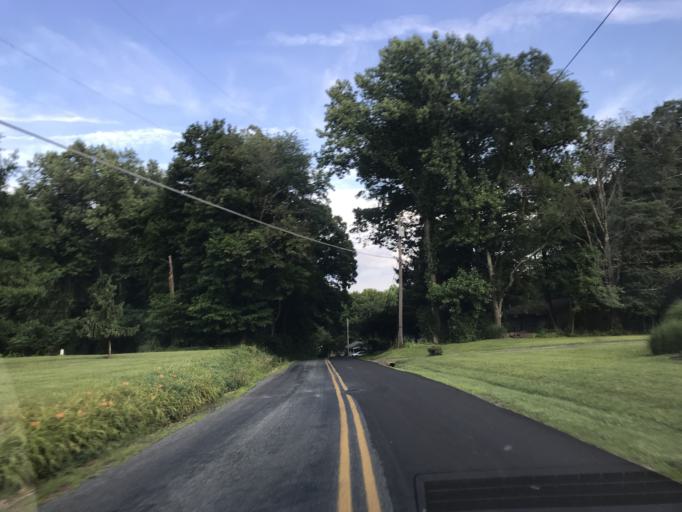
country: US
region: Maryland
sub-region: Harford County
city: Aberdeen
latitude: 39.5241
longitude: -76.2150
